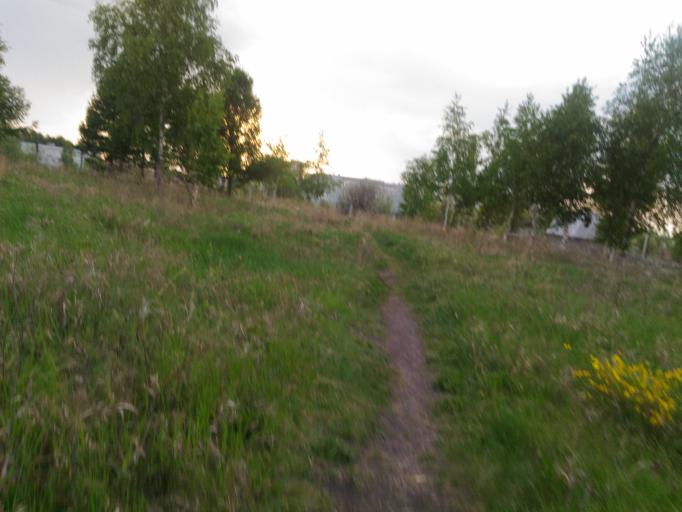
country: RU
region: Ulyanovsk
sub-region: Ulyanovskiy Rayon
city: Ulyanovsk
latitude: 54.3538
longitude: 48.3932
